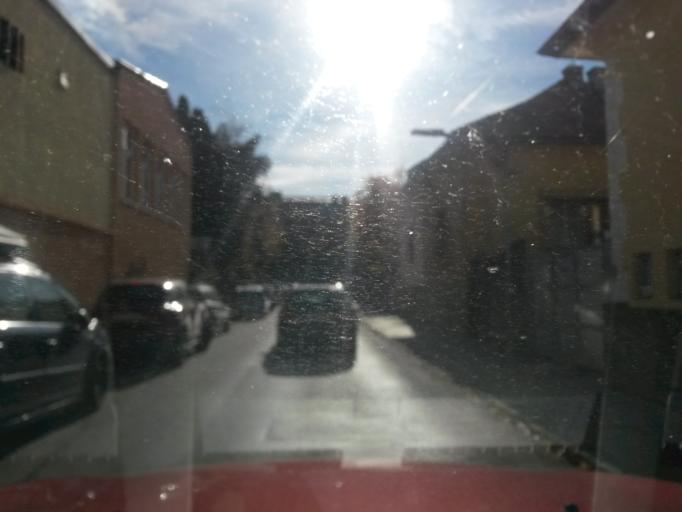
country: SK
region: Presovsky
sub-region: Okres Presov
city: Presov
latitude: 48.9913
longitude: 21.2417
